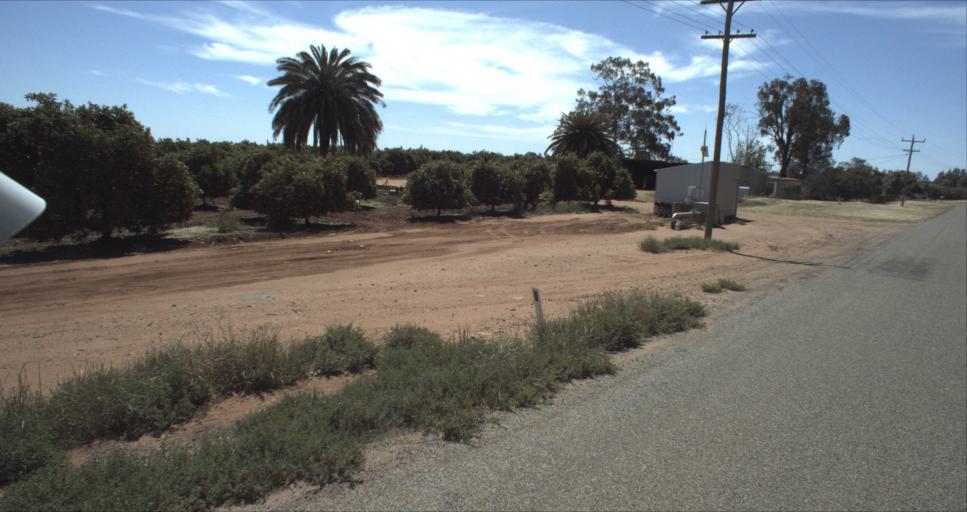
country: AU
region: New South Wales
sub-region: Leeton
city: Leeton
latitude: -34.6043
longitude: 146.4338
